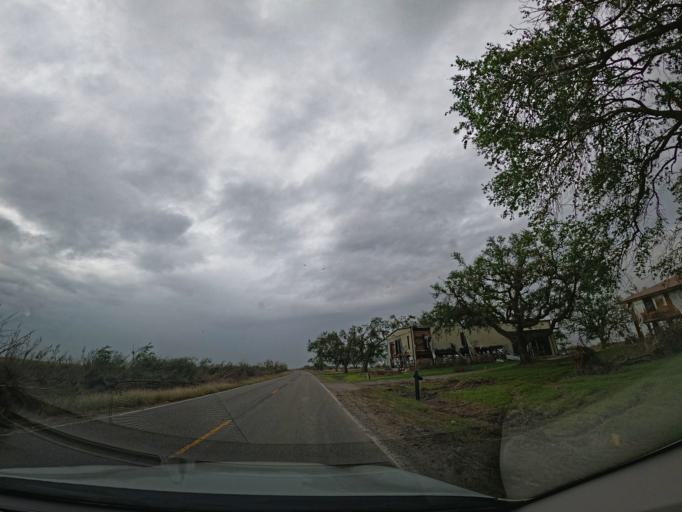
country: US
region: Louisiana
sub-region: Cameron Parish
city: Cameron
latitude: 29.7684
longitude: -92.9863
